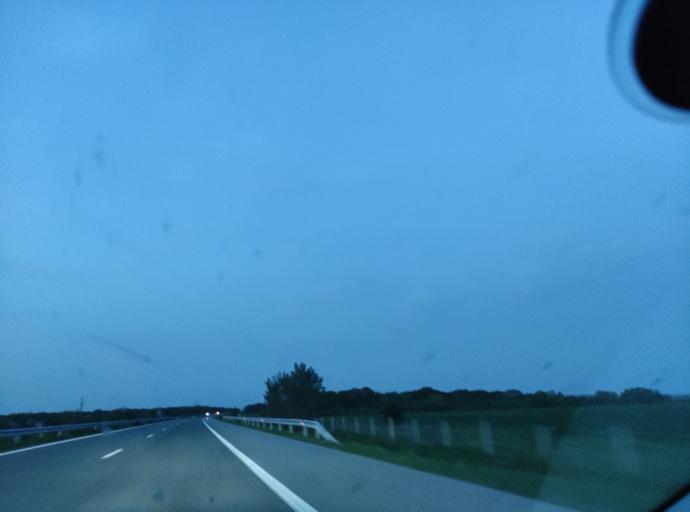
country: BG
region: Stara Zagora
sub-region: Obshtina Stara Zagora
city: Stara Zagora
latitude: 42.3585
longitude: 25.7518
